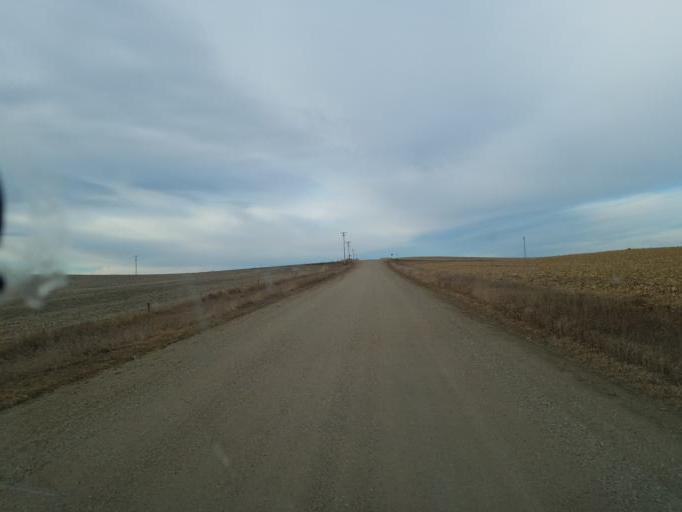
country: US
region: Nebraska
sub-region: Knox County
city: Bloomfield
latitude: 42.5833
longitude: -97.6792
